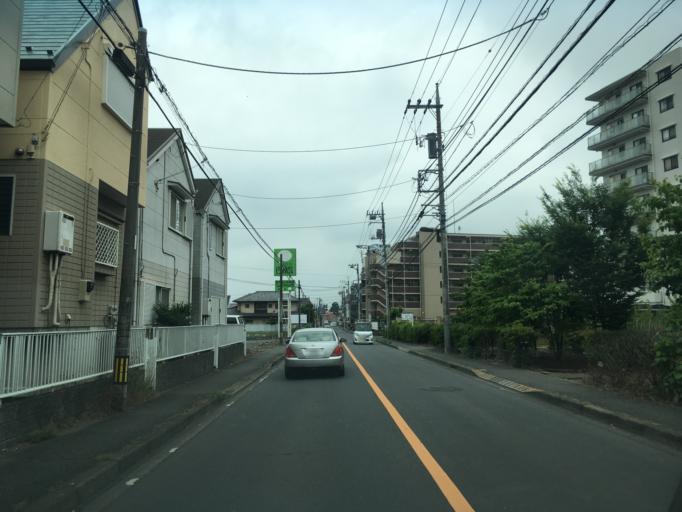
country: JP
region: Tokyo
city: Hino
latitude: 35.7317
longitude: 139.3983
